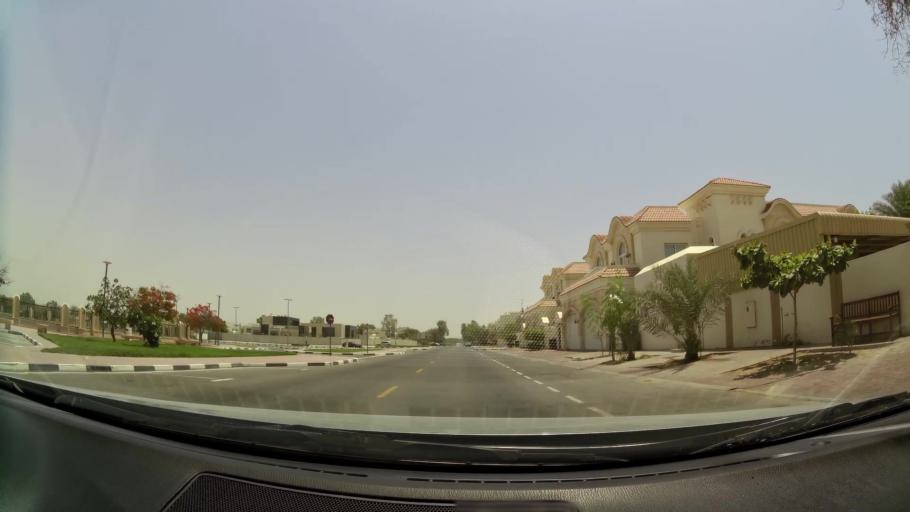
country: AE
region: Dubai
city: Dubai
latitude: 25.1657
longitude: 55.2166
